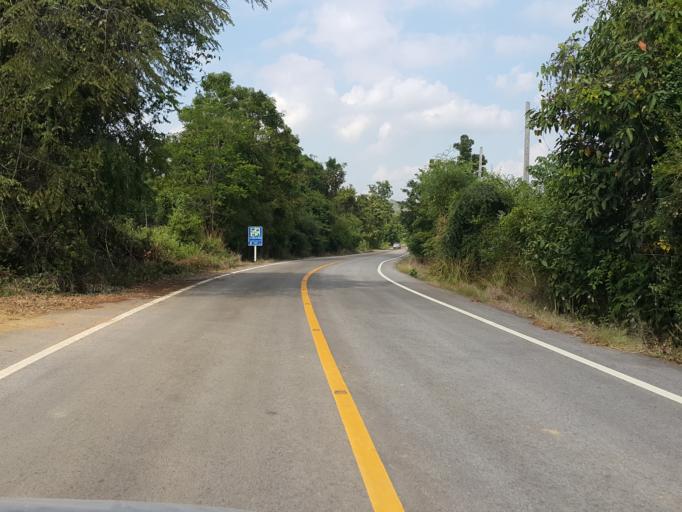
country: TH
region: Sukhothai
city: Thung Saliam
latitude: 17.4380
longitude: 99.5884
